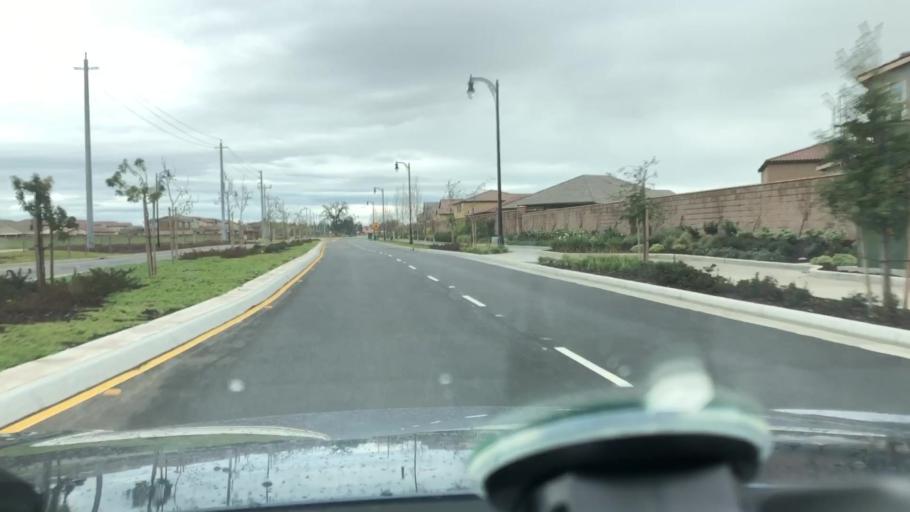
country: US
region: California
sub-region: Sacramento County
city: Elk Grove
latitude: 38.3957
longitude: -121.3978
